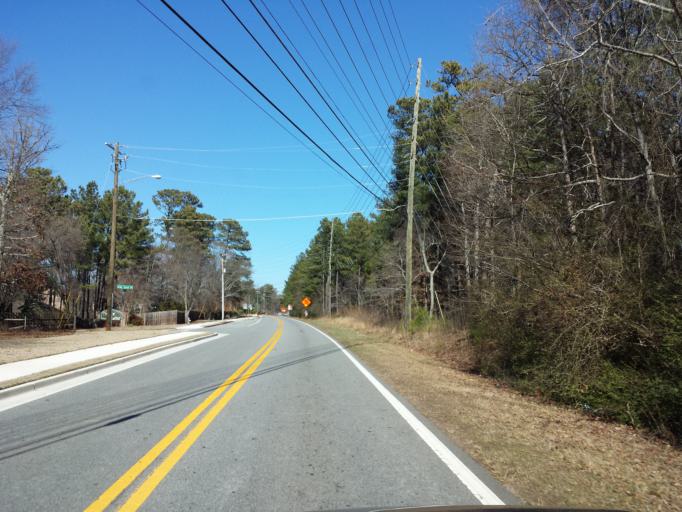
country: US
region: Georgia
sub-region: Cobb County
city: Marietta
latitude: 33.9316
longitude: -84.6126
